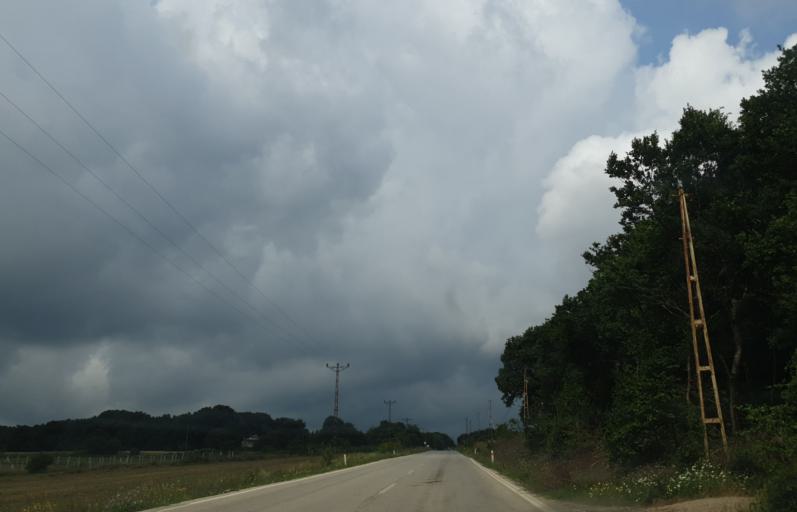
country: TR
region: Tekirdag
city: Saray
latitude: 41.4881
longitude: 27.9693
